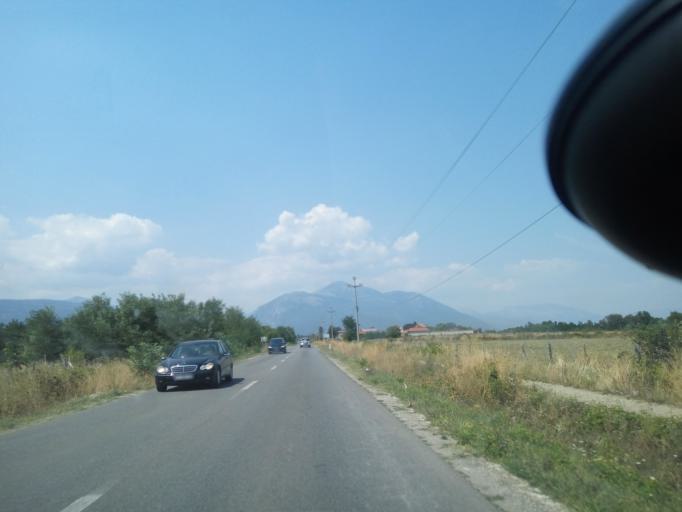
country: XK
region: Gjakova
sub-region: Komuna e Decanit
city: Prilep
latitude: 42.4814
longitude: 20.3327
